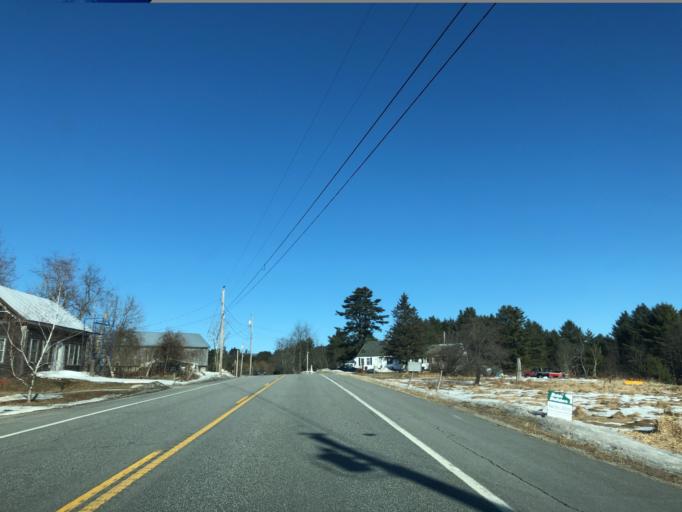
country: US
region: Maine
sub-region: Cumberland County
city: North Windham
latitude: 43.8440
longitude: -70.3840
